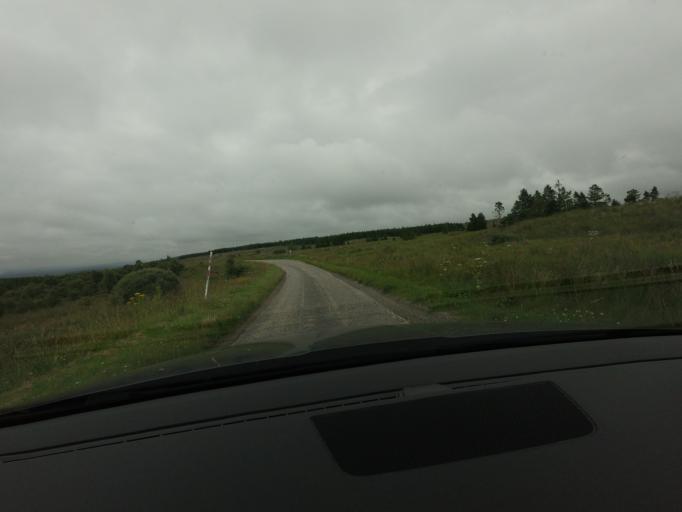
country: GB
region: Scotland
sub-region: Highland
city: Alness
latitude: 58.1366
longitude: -4.4629
